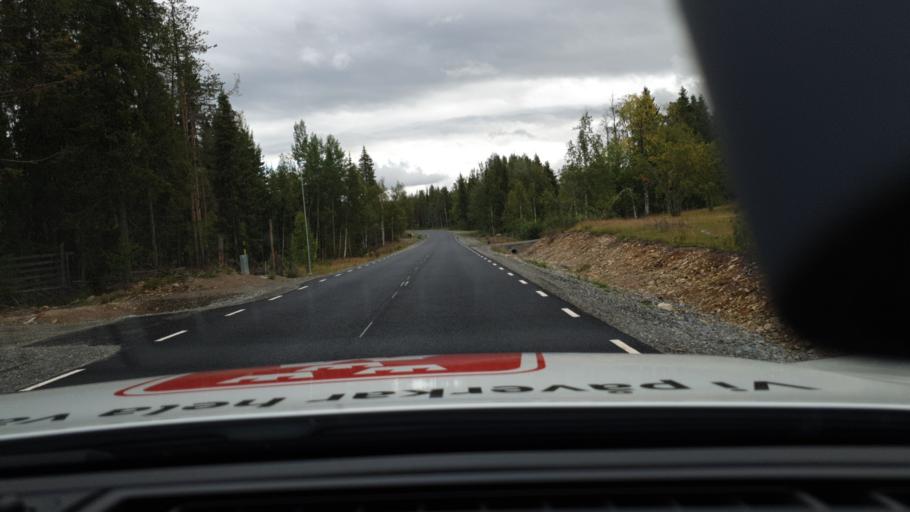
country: SE
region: Norrbotten
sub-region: Gallivare Kommun
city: Gaellivare
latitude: 66.8867
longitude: 21.2831
